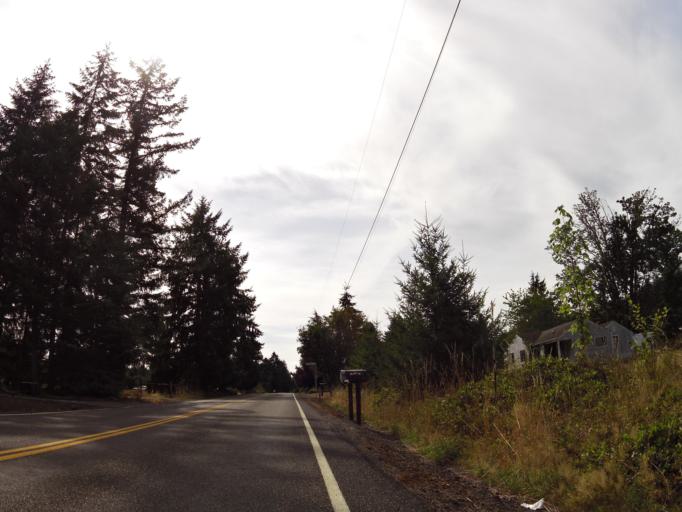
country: US
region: Washington
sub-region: Lewis County
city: Chehalis
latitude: 46.6010
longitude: -122.9712
